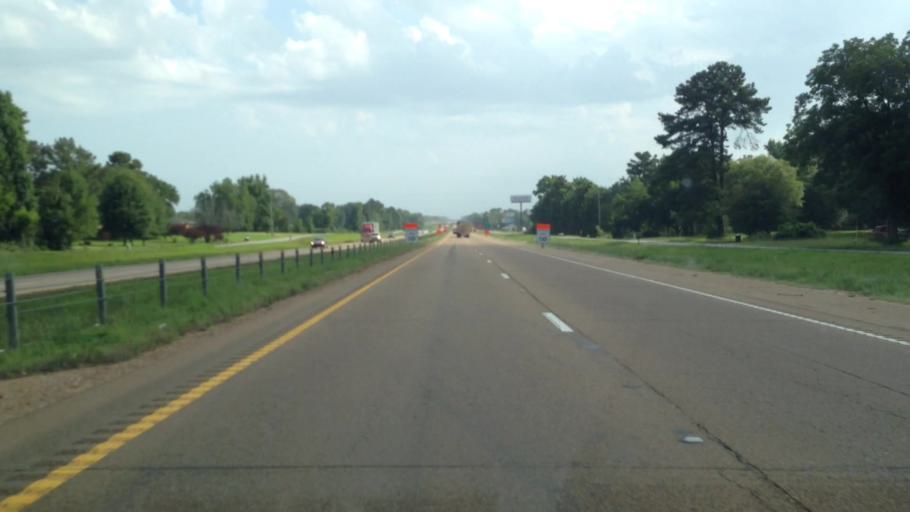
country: US
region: Mississippi
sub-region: Hinds County
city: Terry
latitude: 32.0816
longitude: -90.3127
